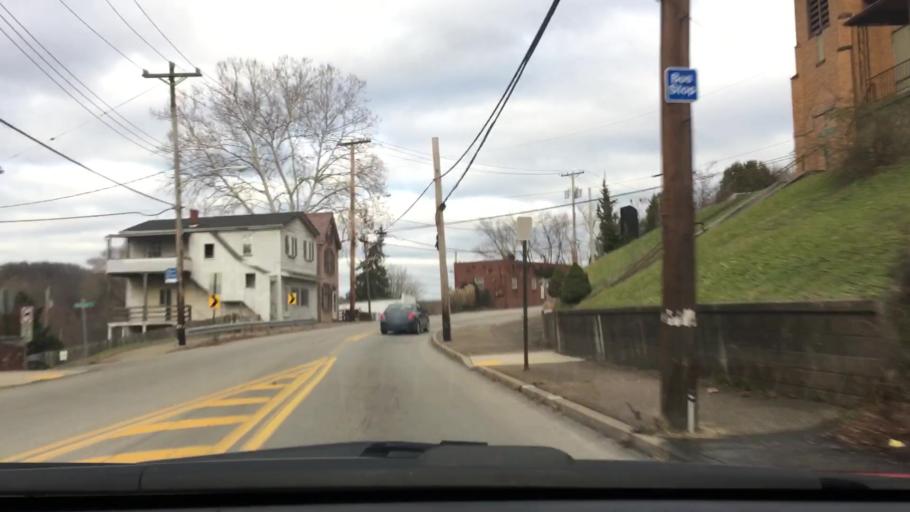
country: US
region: Pennsylvania
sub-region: Allegheny County
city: Versailles
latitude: 40.3164
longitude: -79.8329
